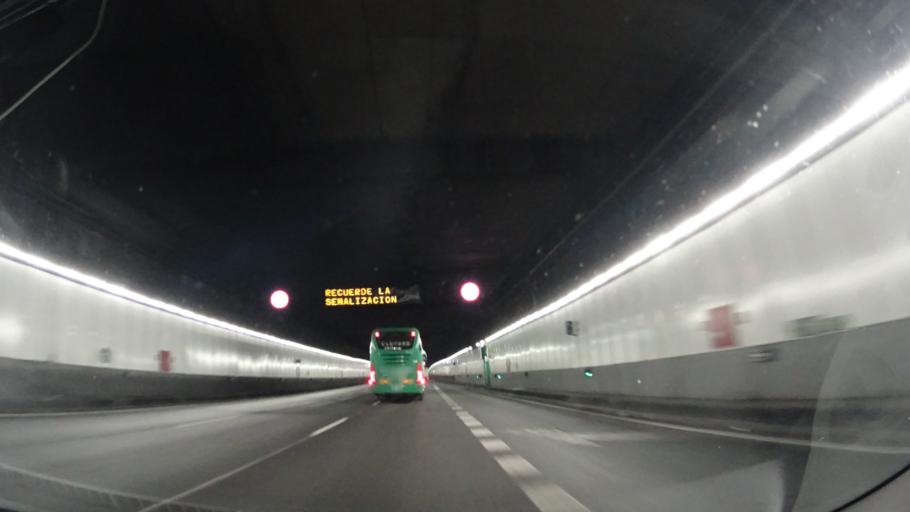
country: ES
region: Madrid
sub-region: Provincia de Madrid
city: Usera
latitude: 40.3923
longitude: -3.7018
